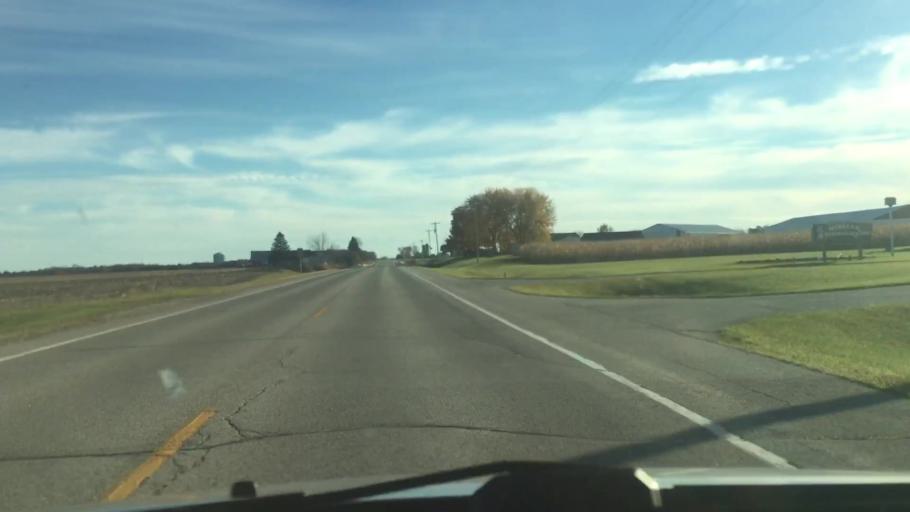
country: US
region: Wisconsin
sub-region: Kewaunee County
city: Kewaunee
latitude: 44.3687
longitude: -87.5424
